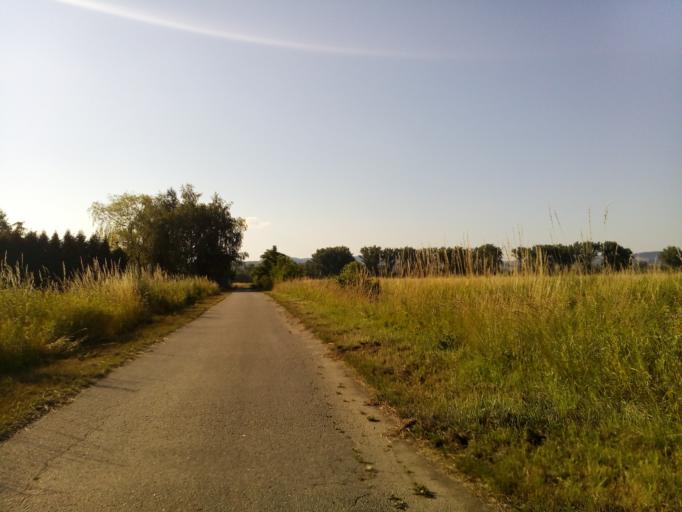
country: PL
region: Lesser Poland Voivodeship
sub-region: Powiat nowosadecki
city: Stary Sacz
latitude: 49.5719
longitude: 20.6246
